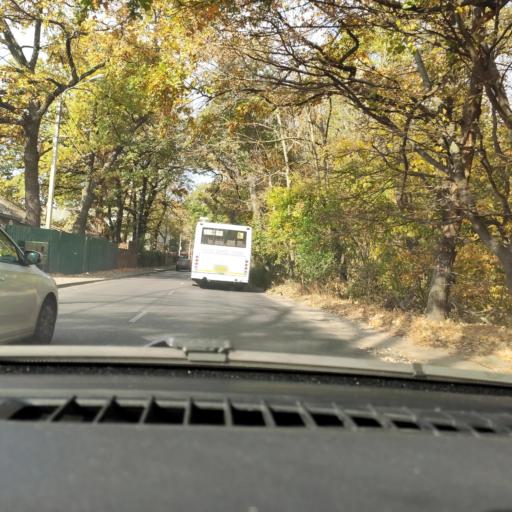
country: RU
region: Voronezj
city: Voronezh
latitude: 51.7243
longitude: 39.2187
